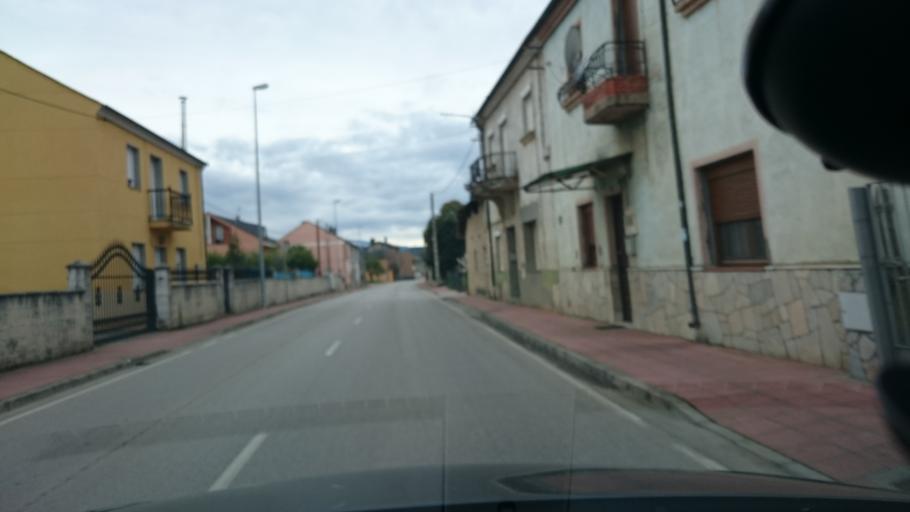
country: ES
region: Castille and Leon
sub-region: Provincia de Leon
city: Carracedelo
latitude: 42.5532
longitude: -6.7346
